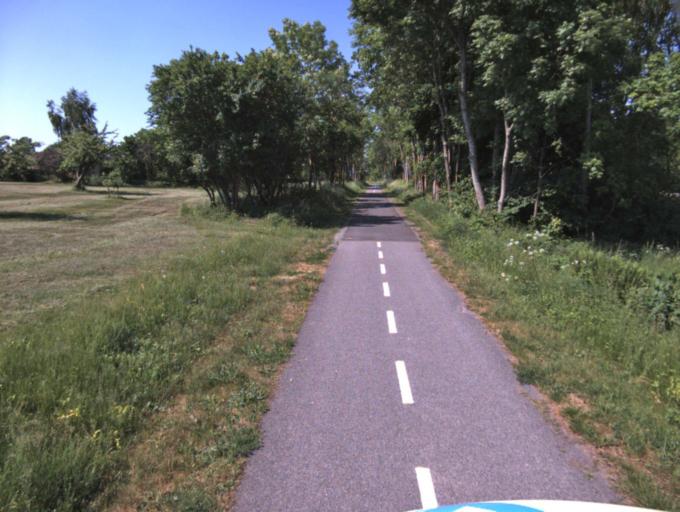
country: SE
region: Skane
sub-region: Kristianstads Kommun
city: Fjalkinge
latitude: 56.0950
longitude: 14.2413
